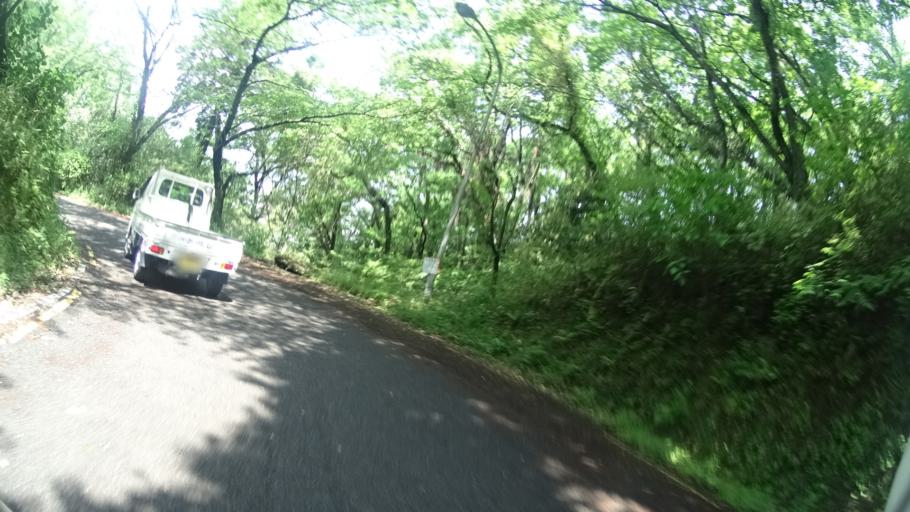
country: JP
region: Tokushima
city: Tokushima-shi
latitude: 34.0688
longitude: 134.5134
